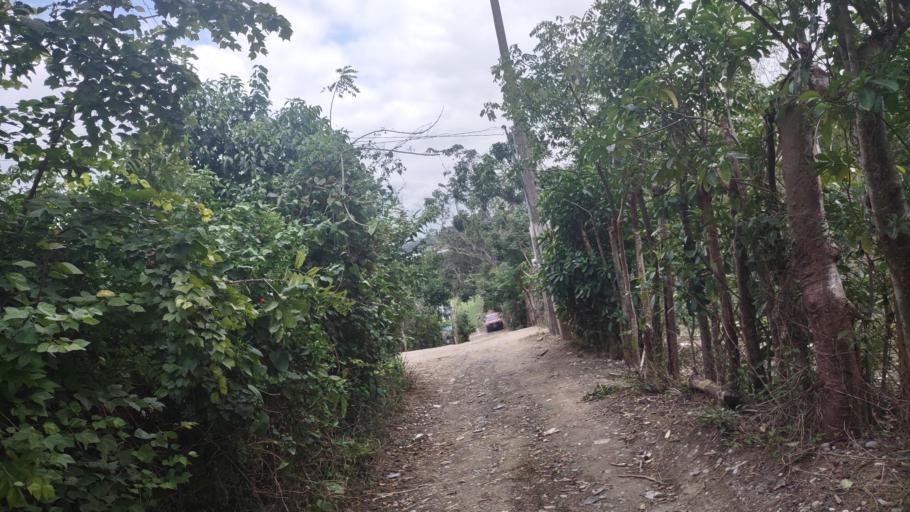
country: MX
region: Veracruz
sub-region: Papantla
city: Polutla
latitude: 20.4641
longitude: -97.2573
